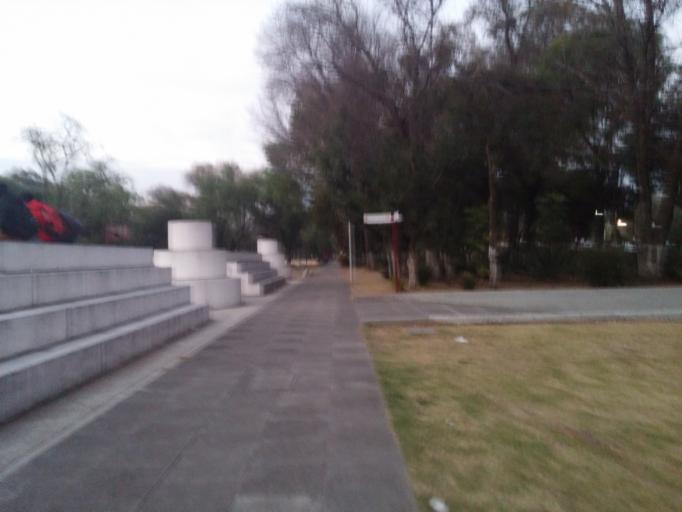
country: MX
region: Mexico
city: Colonia Lindavista
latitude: 19.4996
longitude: -99.1365
